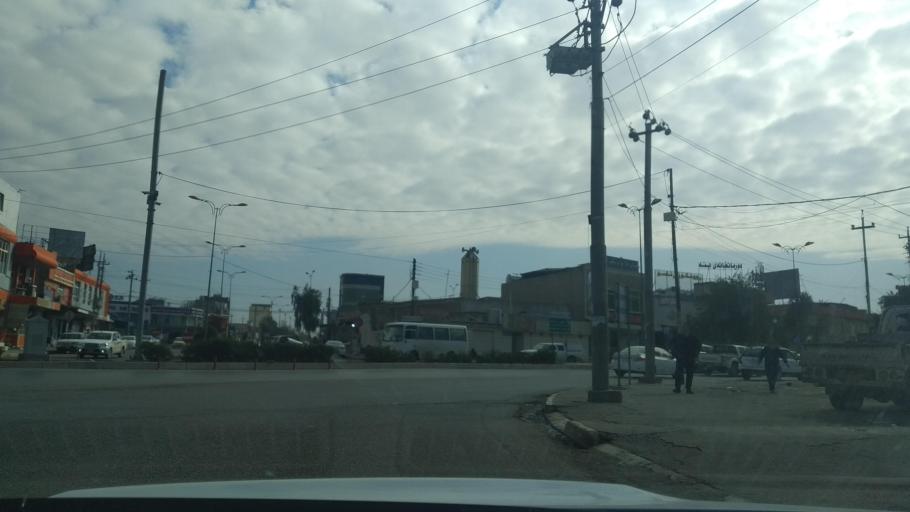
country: IQ
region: Arbil
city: Erbil
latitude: 36.1737
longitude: 44.0363
